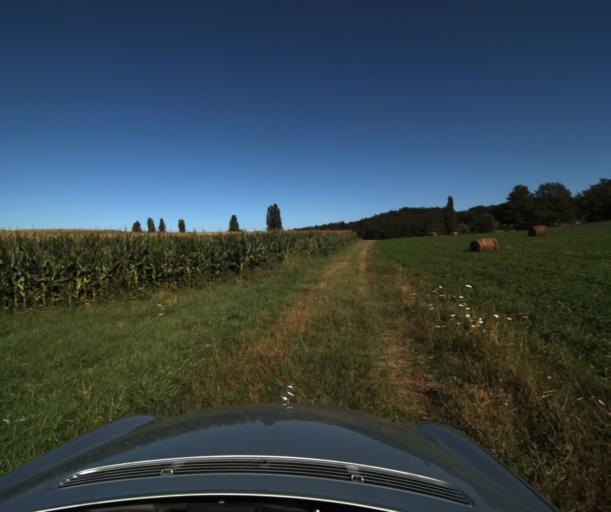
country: FR
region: Midi-Pyrenees
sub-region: Departement de l'Ariege
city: Lavelanet
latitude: 42.9805
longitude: 1.9102
